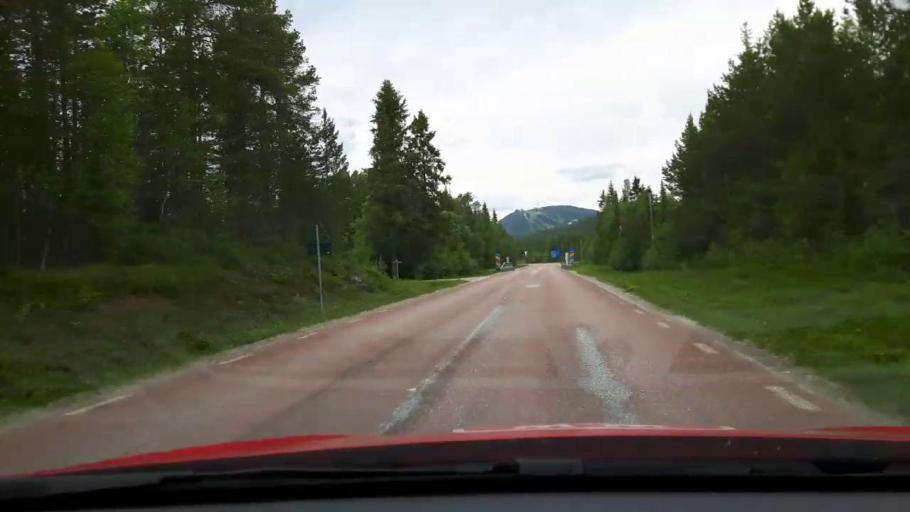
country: NO
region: Hedmark
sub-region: Engerdal
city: Engerdal
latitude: 62.5194
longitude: 12.5959
